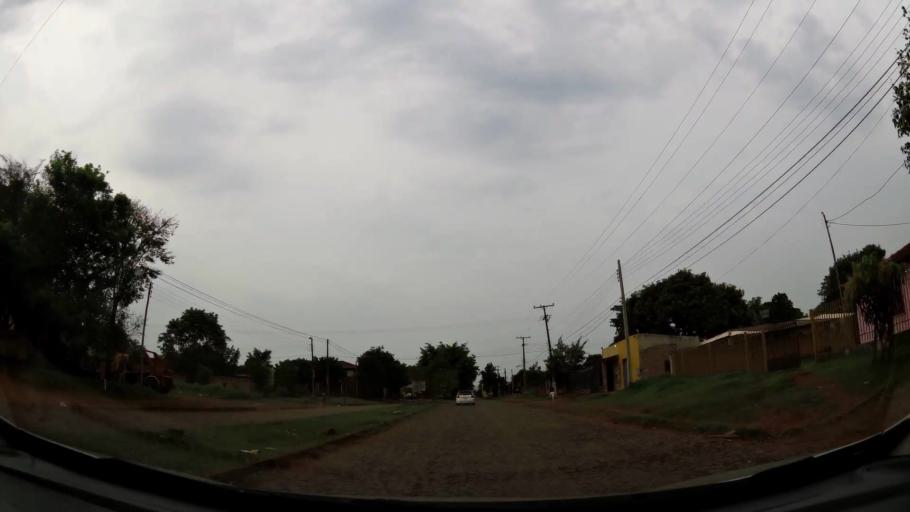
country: PY
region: Alto Parana
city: Presidente Franco
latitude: -25.5341
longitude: -54.6492
